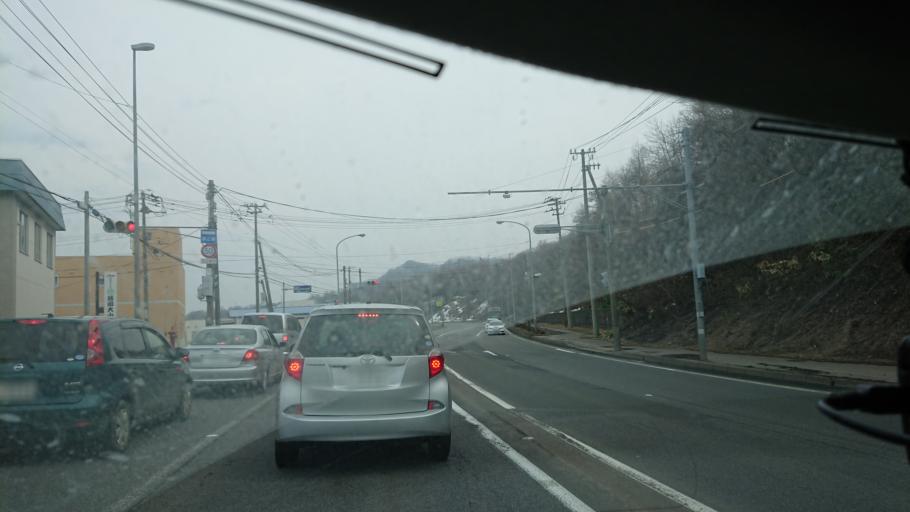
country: JP
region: Hokkaido
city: Otaru
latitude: 43.1392
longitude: 141.1701
